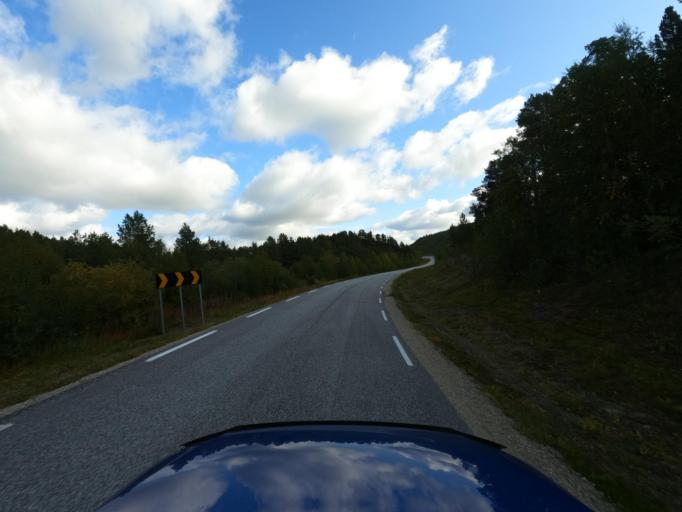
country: NO
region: Finnmark Fylke
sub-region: Karasjok
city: Karasjohka
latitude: 69.4370
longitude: 25.1638
